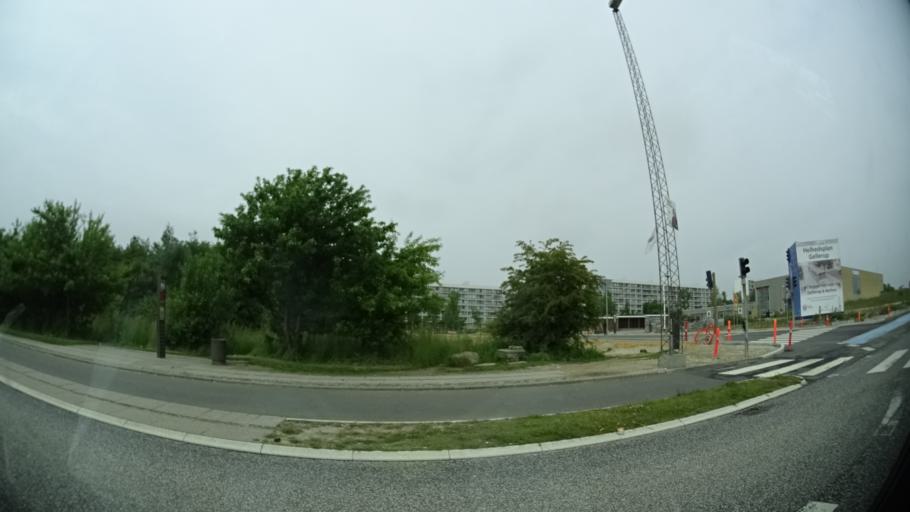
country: DK
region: Central Jutland
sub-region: Arhus Kommune
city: Stavtrup
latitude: 56.1580
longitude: 10.1430
